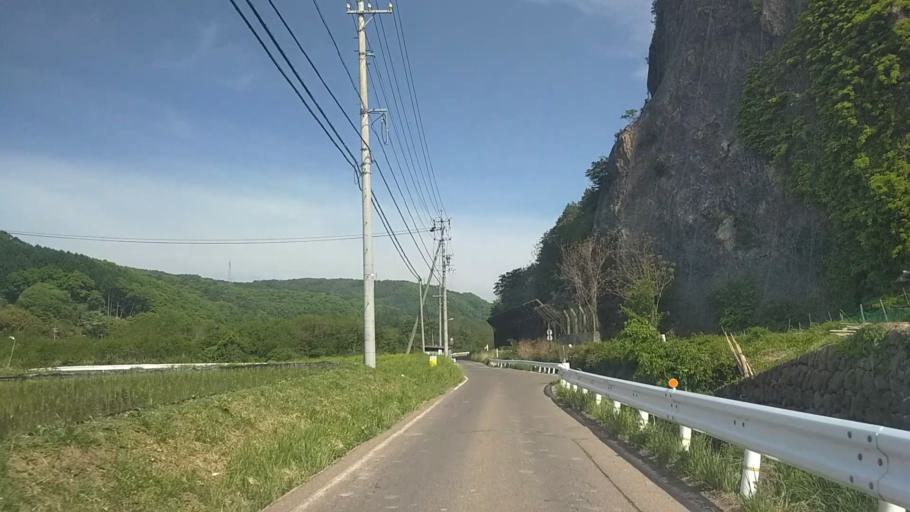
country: JP
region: Nagano
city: Saku
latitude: 36.1089
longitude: 138.4815
